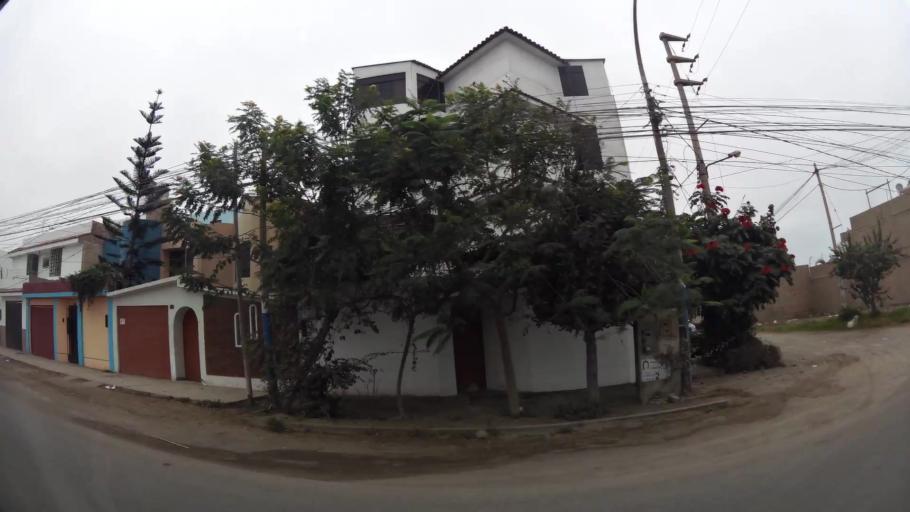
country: PE
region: Ica
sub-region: Provincia de Pisco
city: Pisco
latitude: -13.7170
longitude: -76.2115
